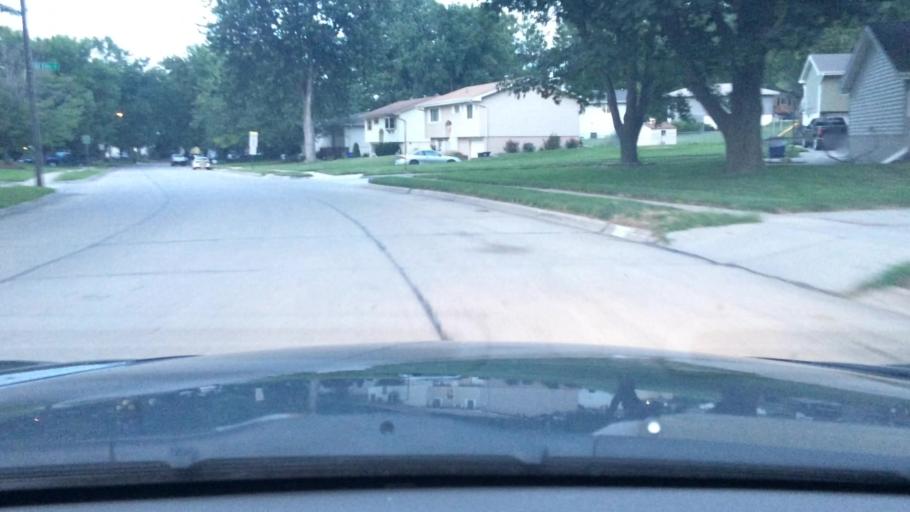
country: US
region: Nebraska
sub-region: Sarpy County
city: La Vista
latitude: 41.1840
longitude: -96.0521
